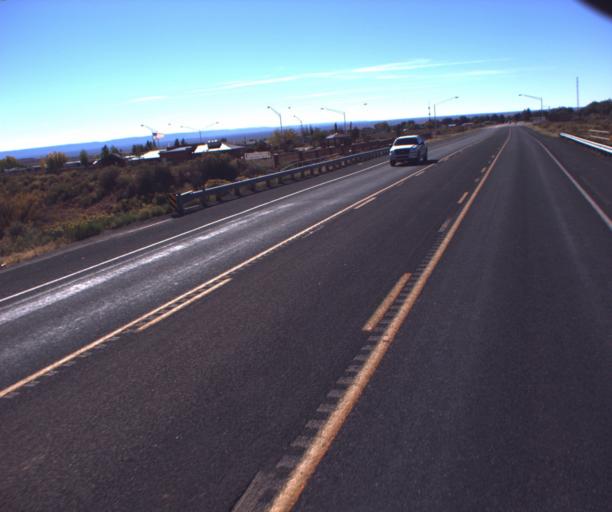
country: US
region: Arizona
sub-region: Coconino County
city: Fredonia
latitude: 36.9641
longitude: -112.5270
